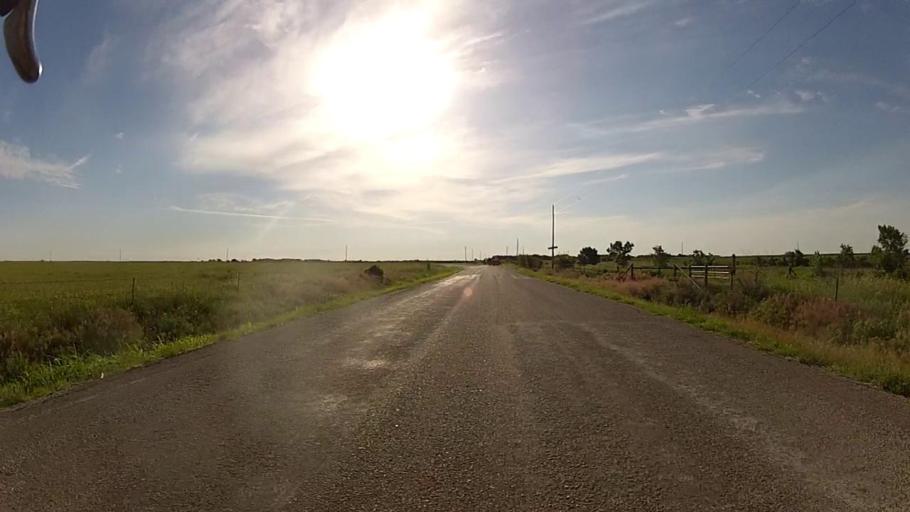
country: US
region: Kansas
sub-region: Cowley County
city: Arkansas City
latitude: 37.0485
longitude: -96.8254
